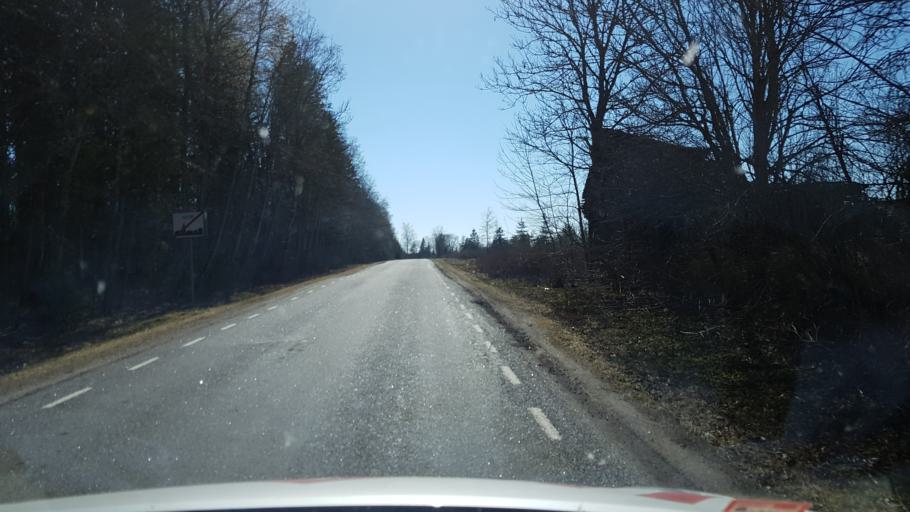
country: EE
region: Laeaene-Virumaa
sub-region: Tamsalu vald
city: Tamsalu
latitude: 59.0840
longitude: 26.1596
